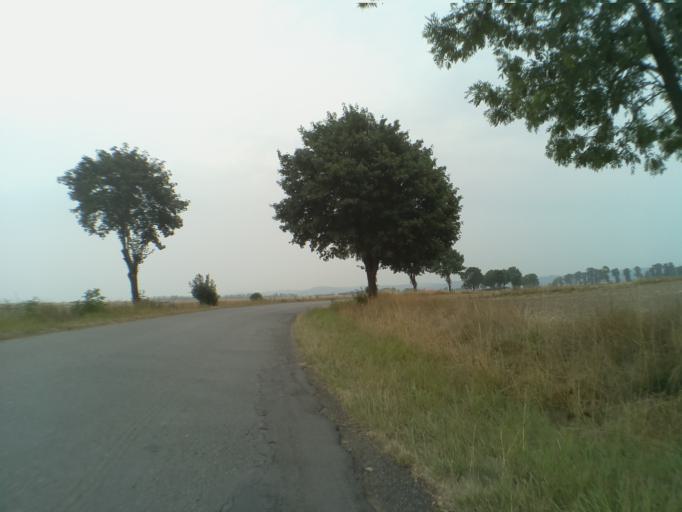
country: PL
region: Lower Silesian Voivodeship
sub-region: Powiat swidnicki
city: Swiebodzice
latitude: 50.8939
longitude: 16.3221
